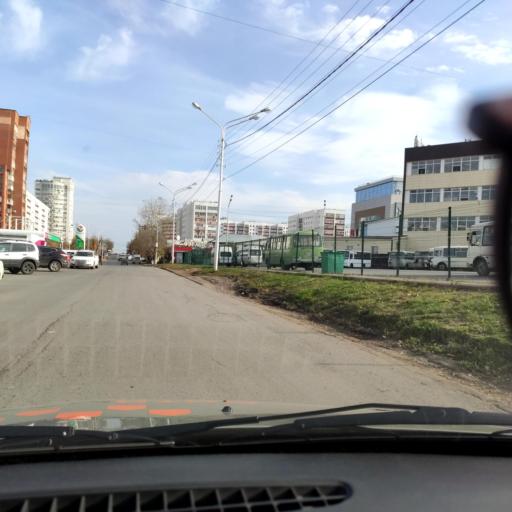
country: RU
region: Bashkortostan
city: Ufa
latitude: 54.7256
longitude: 55.9228
